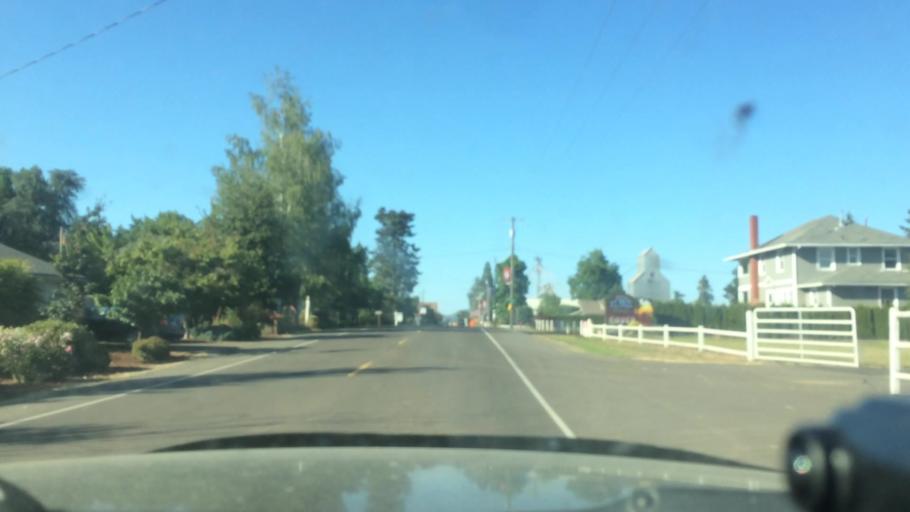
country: US
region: Oregon
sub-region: Yamhill County
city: Dundee
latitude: 45.2074
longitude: -122.9793
